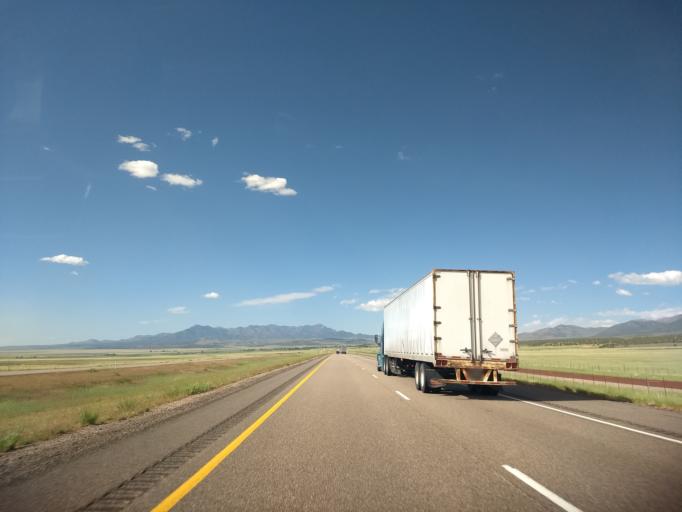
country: US
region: Utah
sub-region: Millard County
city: Fillmore
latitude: 39.0522
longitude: -112.2900
